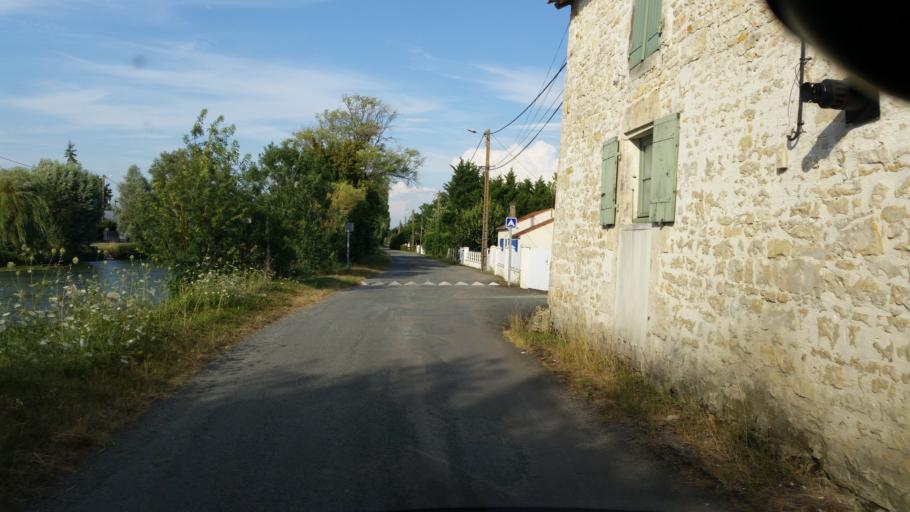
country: FR
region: Poitou-Charentes
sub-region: Departement de la Charente-Maritime
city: Marans
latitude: 46.3166
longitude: -0.9766
